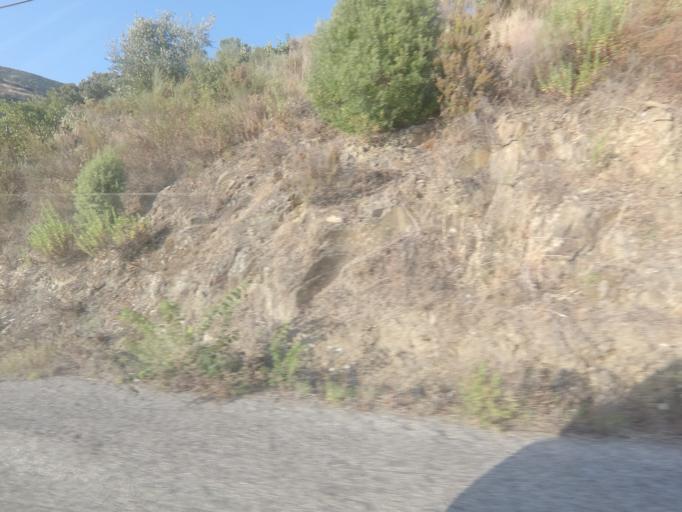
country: PT
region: Viseu
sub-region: Armamar
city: Armamar
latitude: 41.1291
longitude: -7.6736
